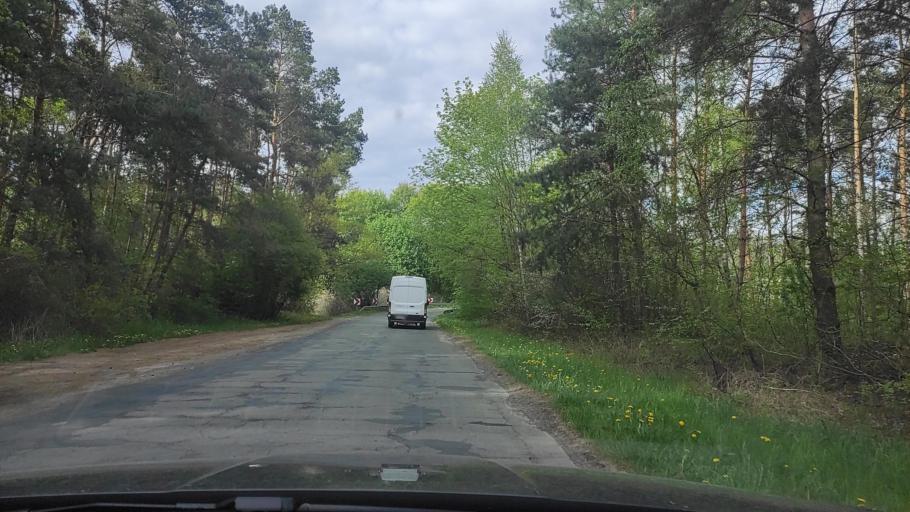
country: PL
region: Greater Poland Voivodeship
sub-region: Powiat poznanski
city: Kostrzyn
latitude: 52.4550
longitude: 17.1631
